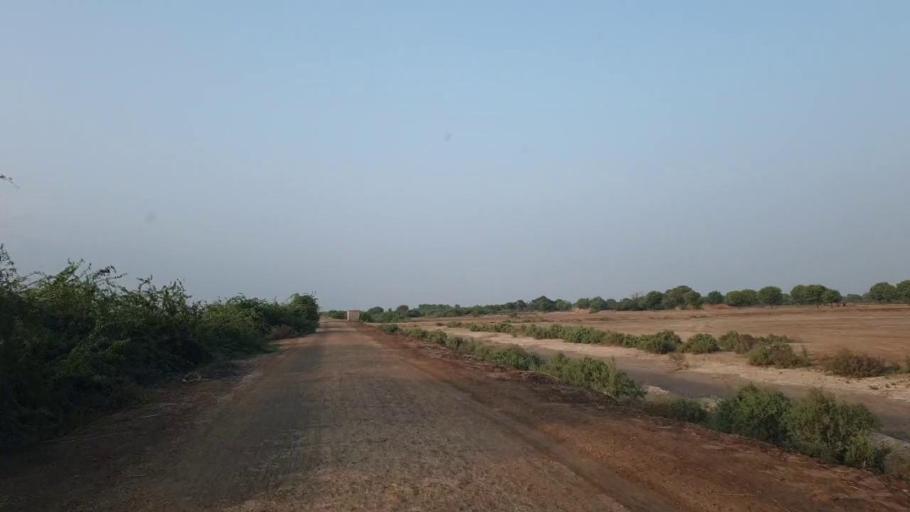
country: PK
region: Sindh
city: Tando Ghulam Ali
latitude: 25.0598
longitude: 68.9605
